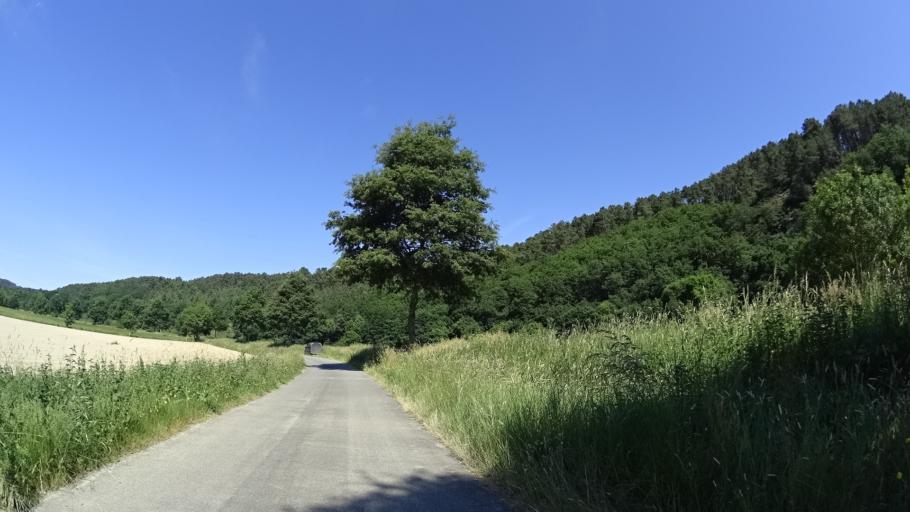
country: FR
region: Brittany
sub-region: Departement d'Ille-et-Vilaine
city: Langon
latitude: 47.7664
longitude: -1.8234
